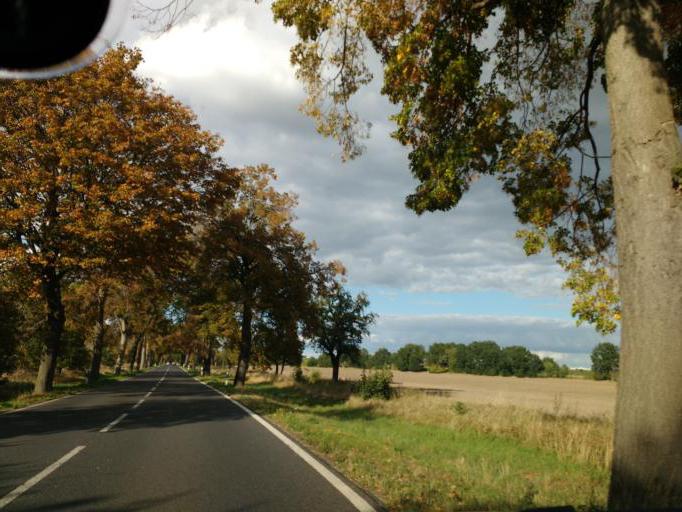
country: DE
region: Berlin
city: Lichtenrade
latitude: 52.3665
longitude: 13.4418
